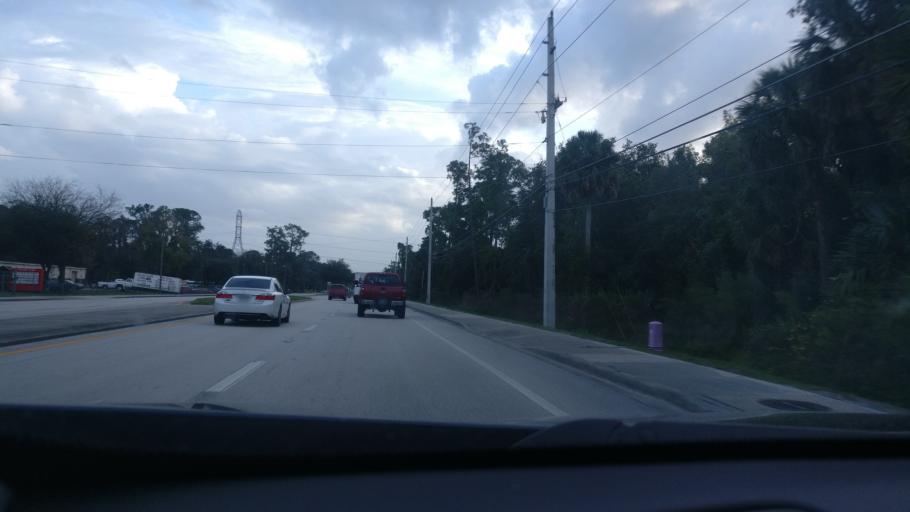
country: US
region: Florida
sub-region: Volusia County
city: DeBary
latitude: 28.8522
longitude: -81.3223
